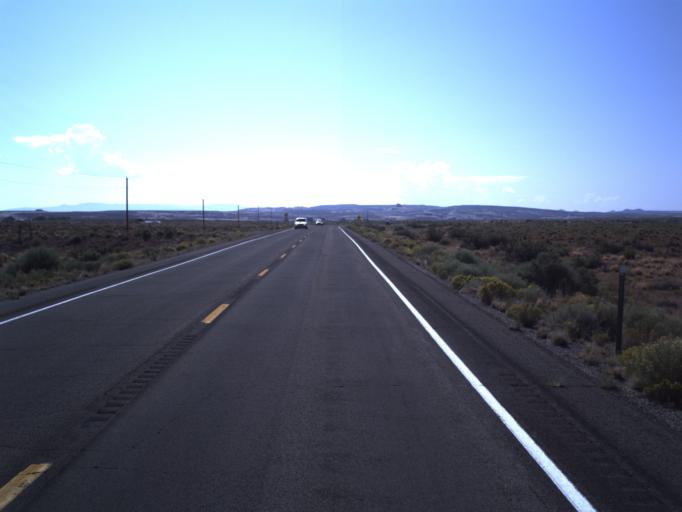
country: US
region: Utah
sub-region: San Juan County
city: Blanding
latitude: 37.1270
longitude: -109.5480
